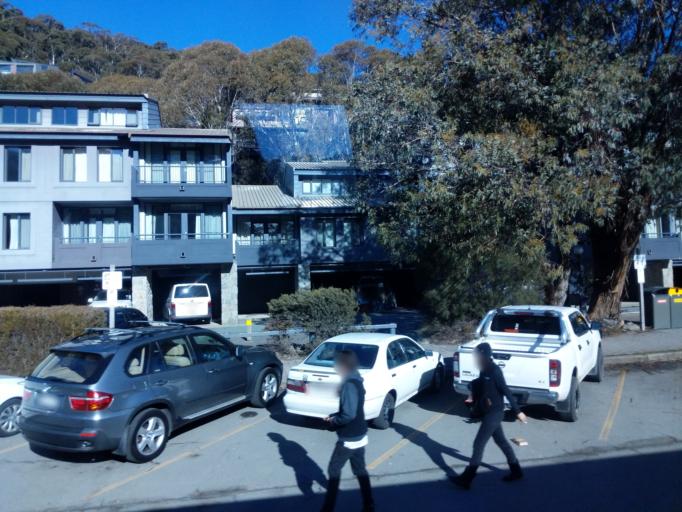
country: AU
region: New South Wales
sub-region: Snowy River
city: Jindabyne
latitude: -36.5036
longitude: 148.3062
